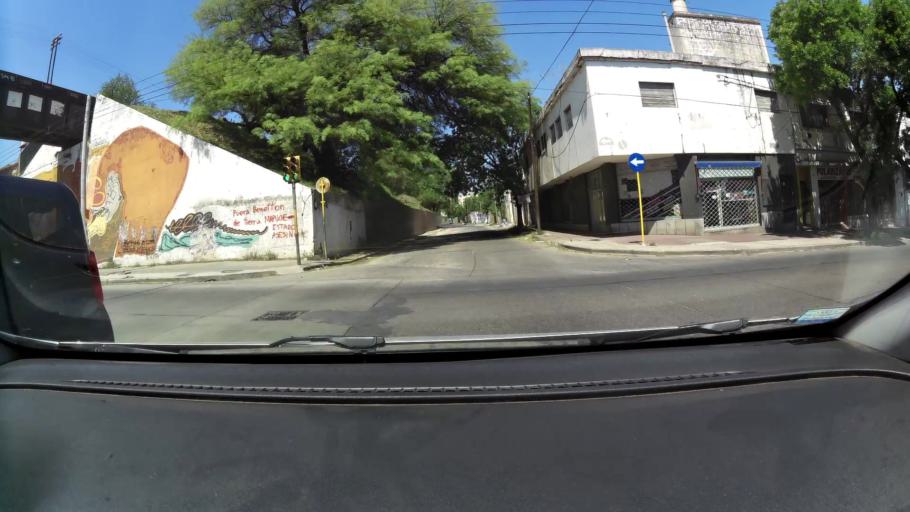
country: AR
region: Cordoba
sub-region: Departamento de Capital
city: Cordoba
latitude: -31.4038
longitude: -64.1875
